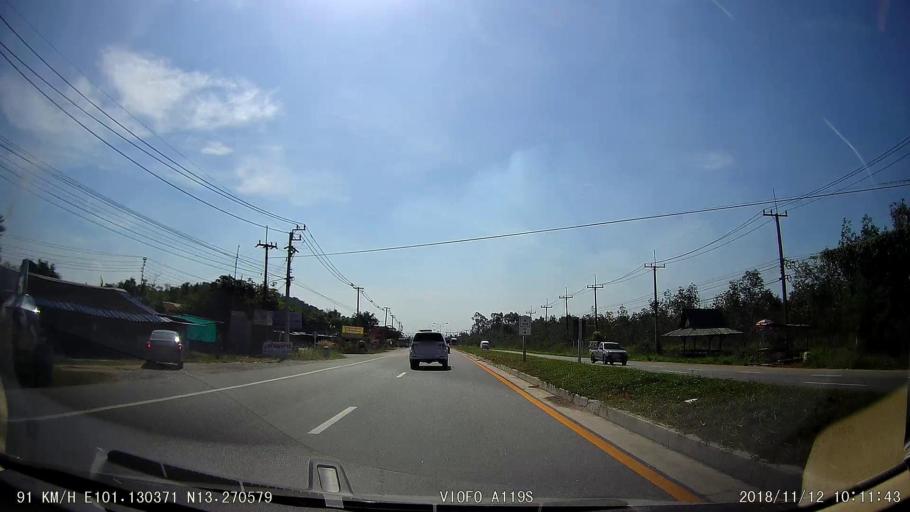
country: TH
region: Chon Buri
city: Ban Bueng
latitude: 13.2703
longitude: 101.1305
